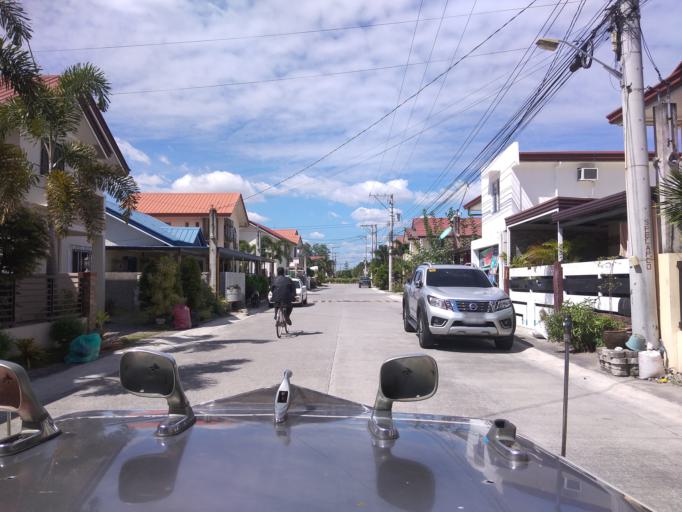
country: PH
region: Central Luzon
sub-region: Province of Pampanga
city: Magliman
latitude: 15.0399
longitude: 120.6550
